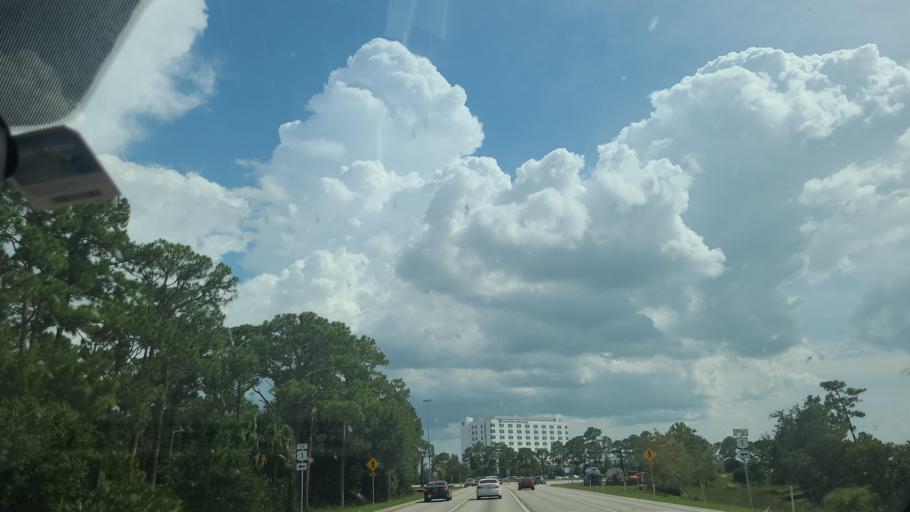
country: US
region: Florida
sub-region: Saint Lucie County
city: Port Saint Lucie
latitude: 27.2661
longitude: -80.4245
